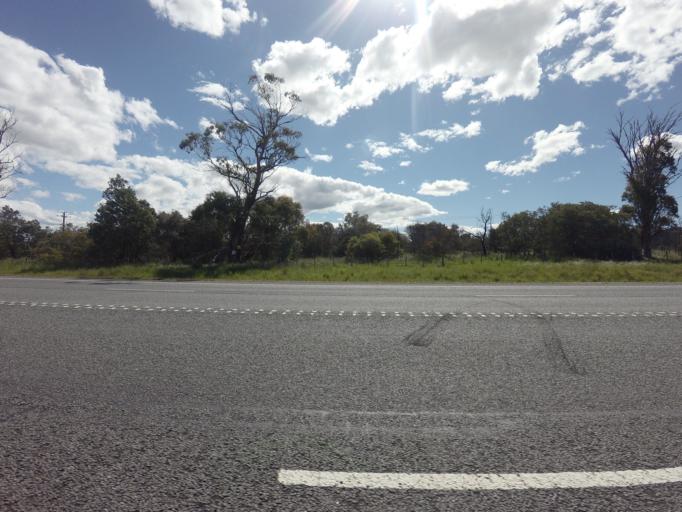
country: AU
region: Tasmania
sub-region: Northern Midlands
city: Evandale
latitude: -41.9997
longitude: 147.5008
